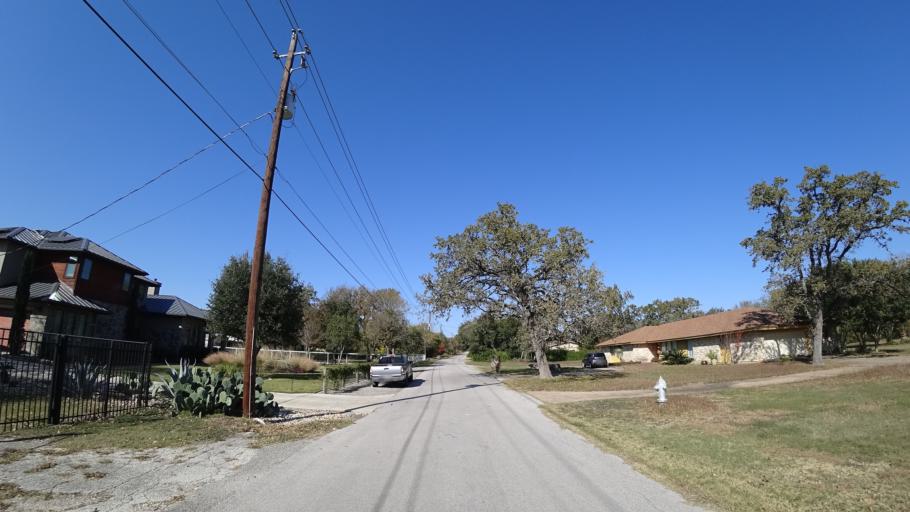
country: US
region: Texas
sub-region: Travis County
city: Barton Creek
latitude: 30.2270
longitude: -97.8565
